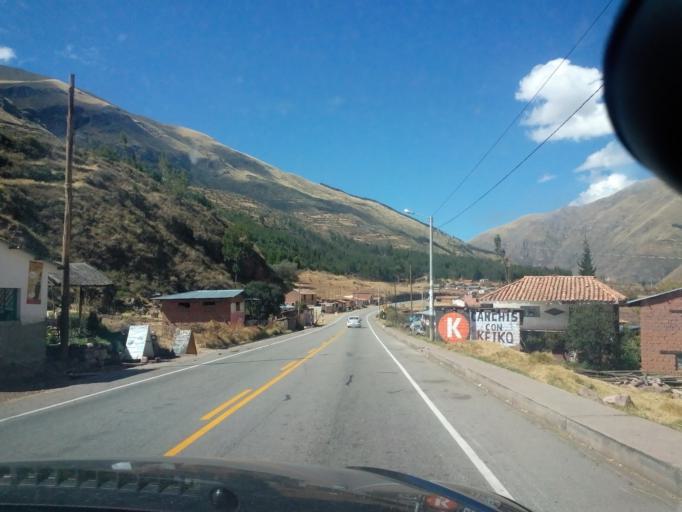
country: PE
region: Cusco
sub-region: Provincia de Quispicanchis
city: Cusipata
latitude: -13.9583
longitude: -71.4974
